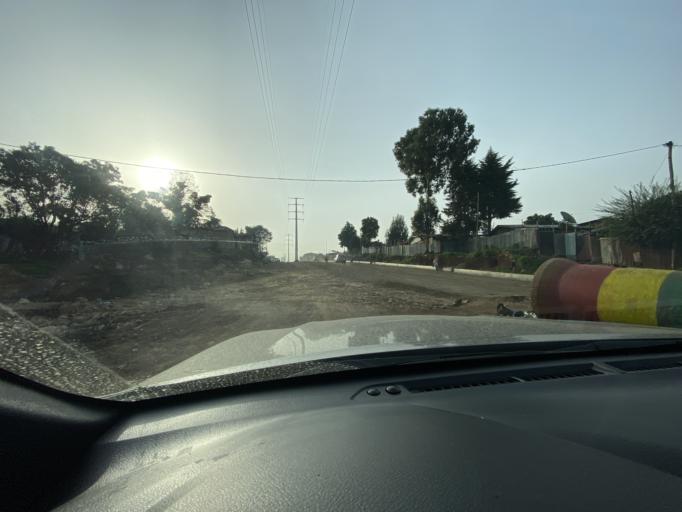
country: ET
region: Adis Abeba
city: Addis Ababa
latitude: 9.0164
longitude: 38.7305
